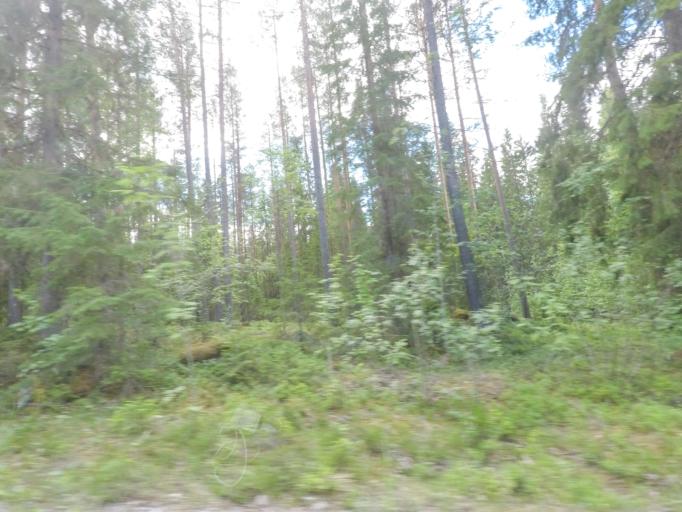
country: FI
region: Central Finland
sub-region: Jyvaeskylae
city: Hankasalmi
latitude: 62.4102
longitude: 26.6476
